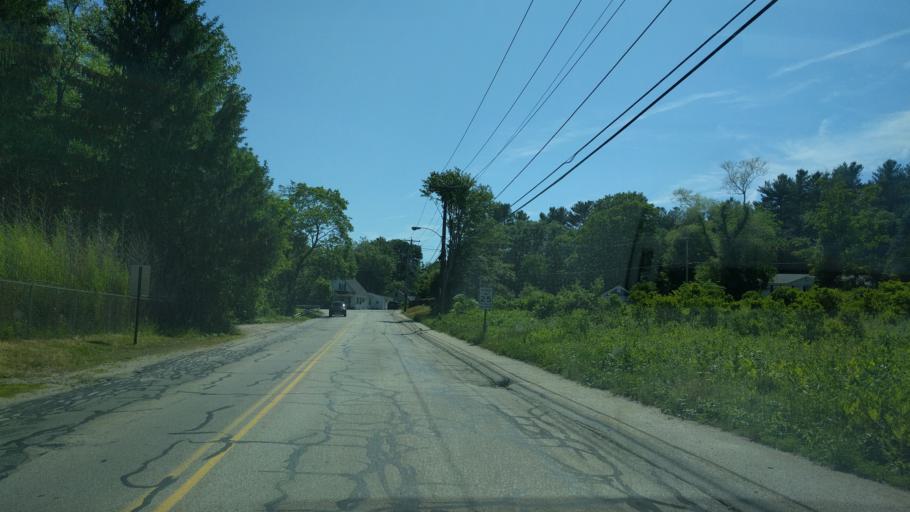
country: US
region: Massachusetts
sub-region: Worcester County
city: East Douglas
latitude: 42.0788
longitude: -71.7079
